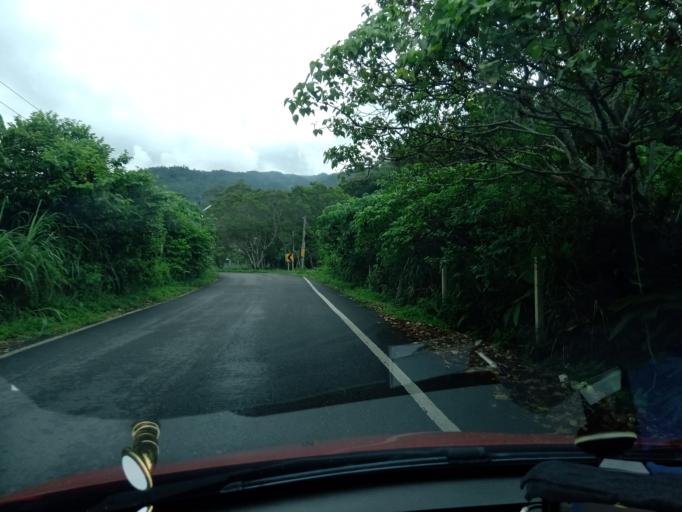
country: TW
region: Taiwan
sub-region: Yilan
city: Yilan
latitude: 24.7812
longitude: 121.7187
